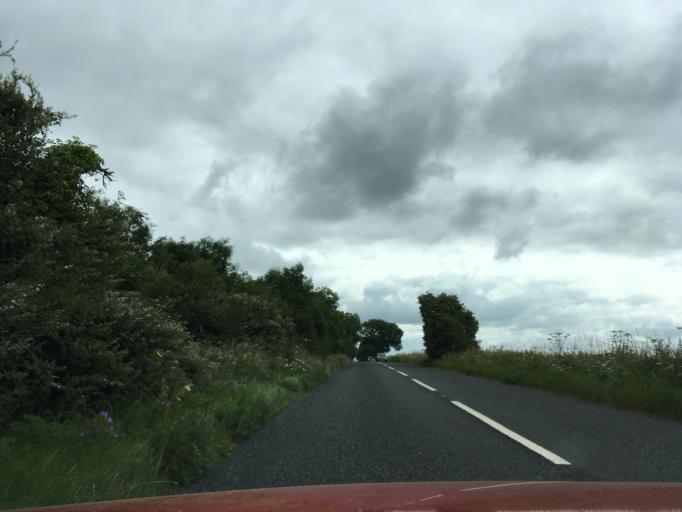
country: GB
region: England
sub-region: Gloucestershire
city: Westfield
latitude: 51.8884
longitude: -1.8541
